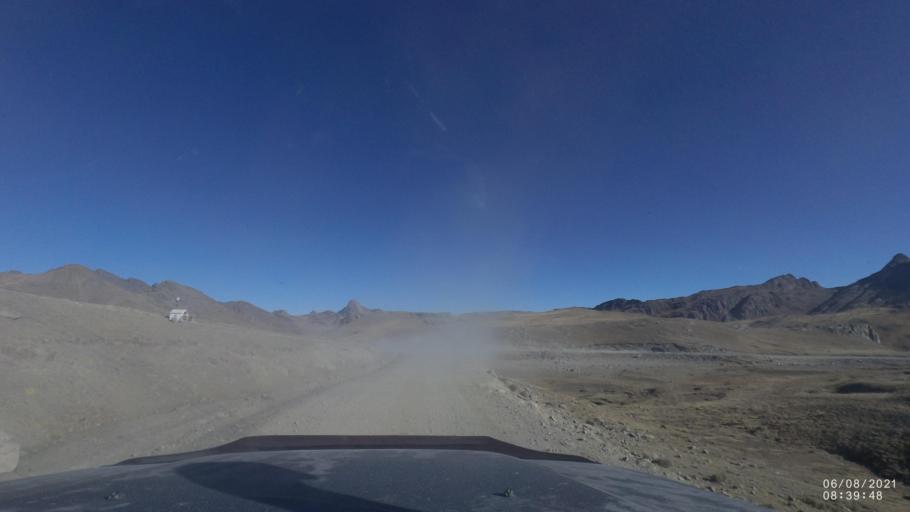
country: BO
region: Cochabamba
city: Sipe Sipe
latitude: -17.1753
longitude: -66.3999
